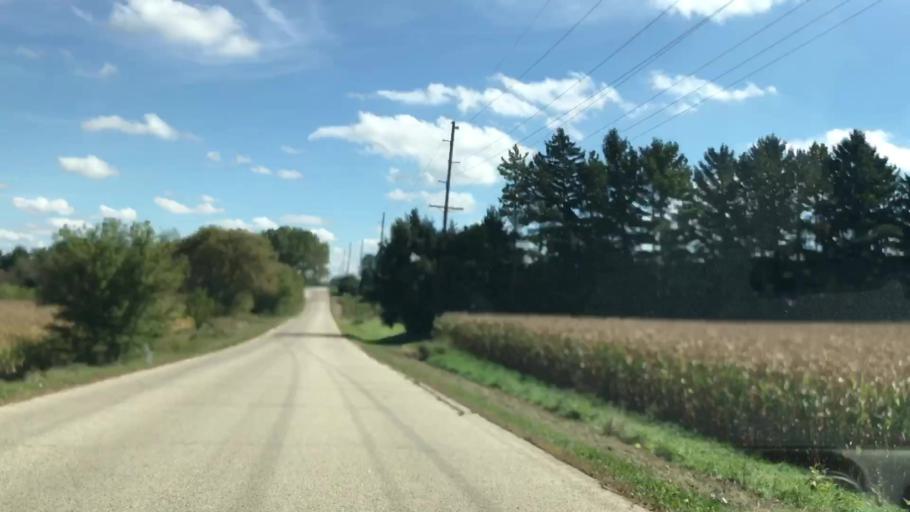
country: US
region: Wisconsin
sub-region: Dodge County
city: Mayville
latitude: 43.5014
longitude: -88.5702
